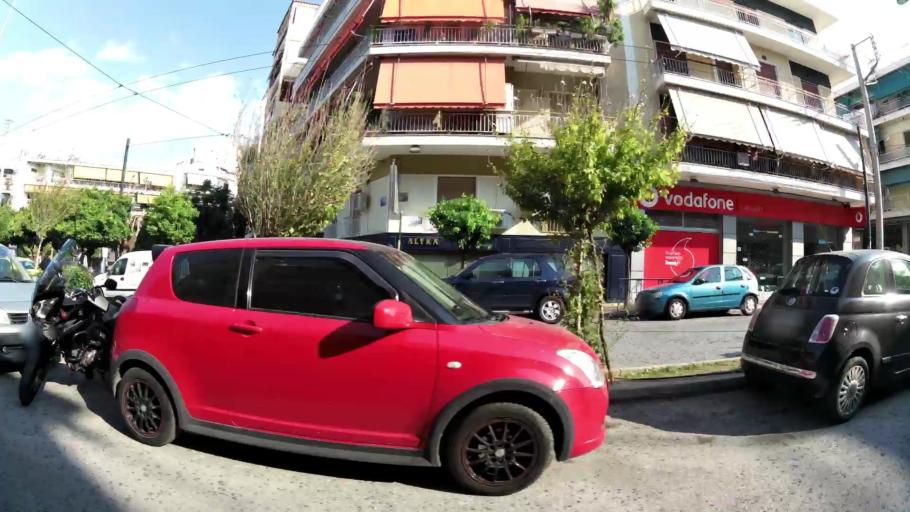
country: GR
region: Attica
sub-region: Nomarchia Athinas
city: Galatsi
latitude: 38.0224
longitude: 23.7502
